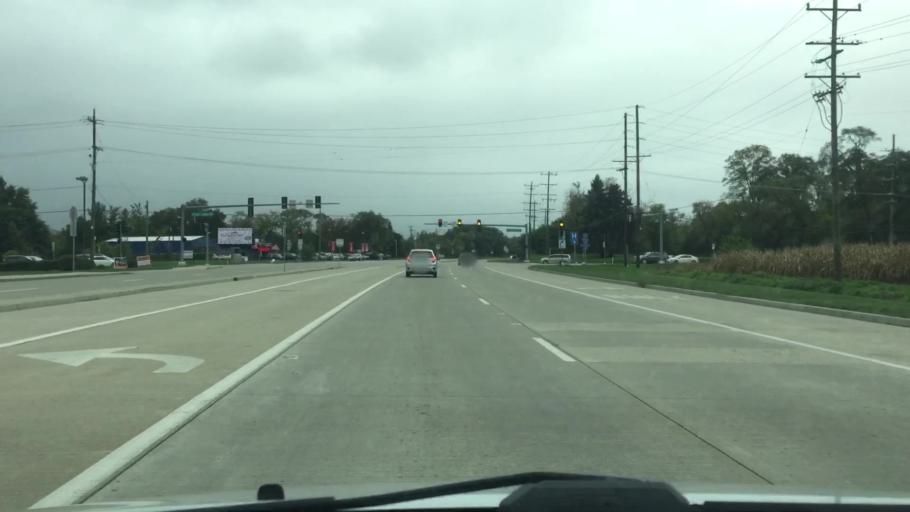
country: US
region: Illinois
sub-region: McHenry County
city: McHenry
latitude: 42.3221
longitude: -88.2744
